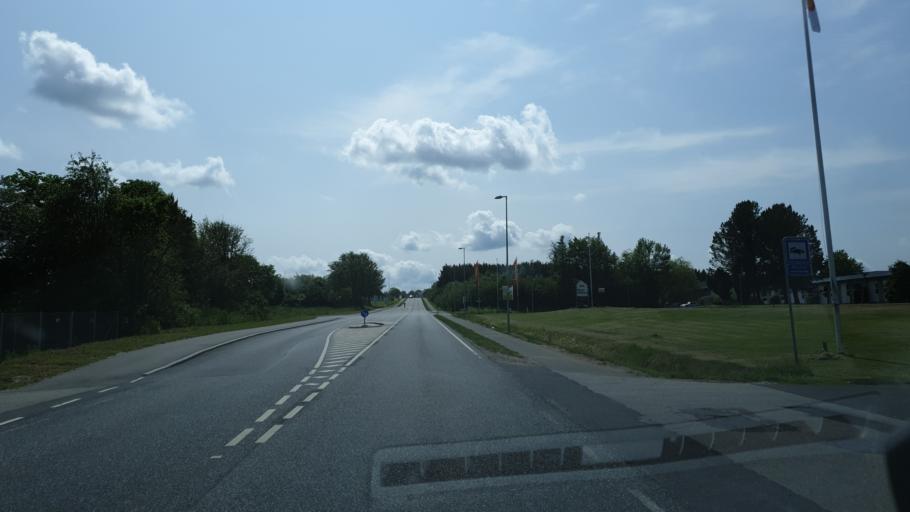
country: DK
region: Central Jutland
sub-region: Favrskov Kommune
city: Hadsten
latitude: 56.3184
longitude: 10.0429
